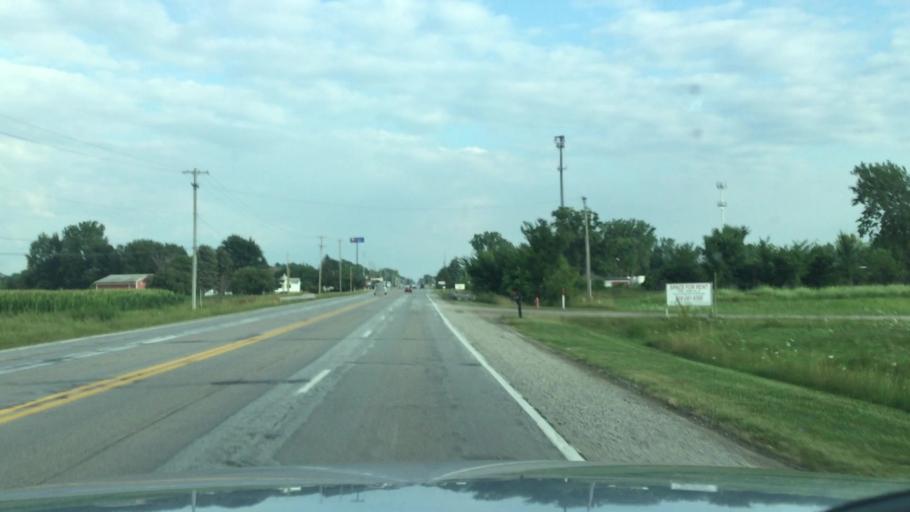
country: US
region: Michigan
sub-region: Saginaw County
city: Birch Run
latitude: 43.2557
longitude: -83.7736
